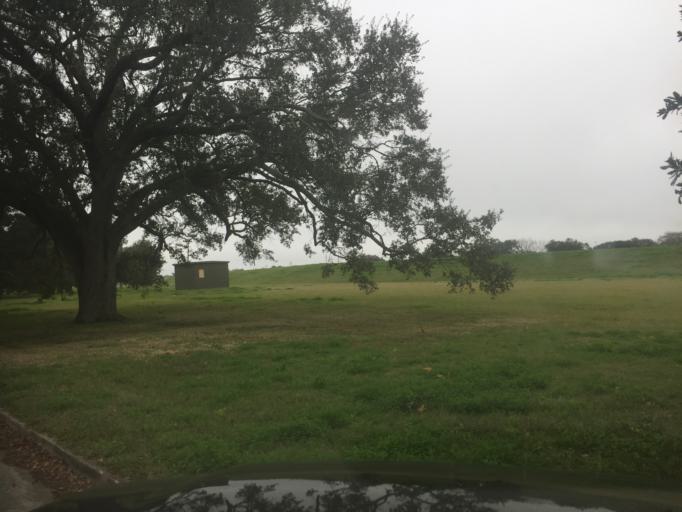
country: US
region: Louisiana
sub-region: Jefferson Parish
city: Metairie
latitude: 30.0219
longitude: -90.0971
